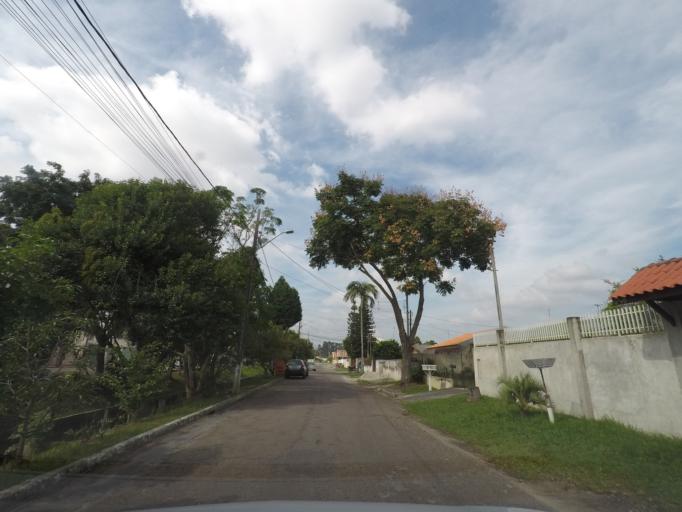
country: BR
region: Parana
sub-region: Pinhais
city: Pinhais
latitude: -25.4733
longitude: -49.1930
